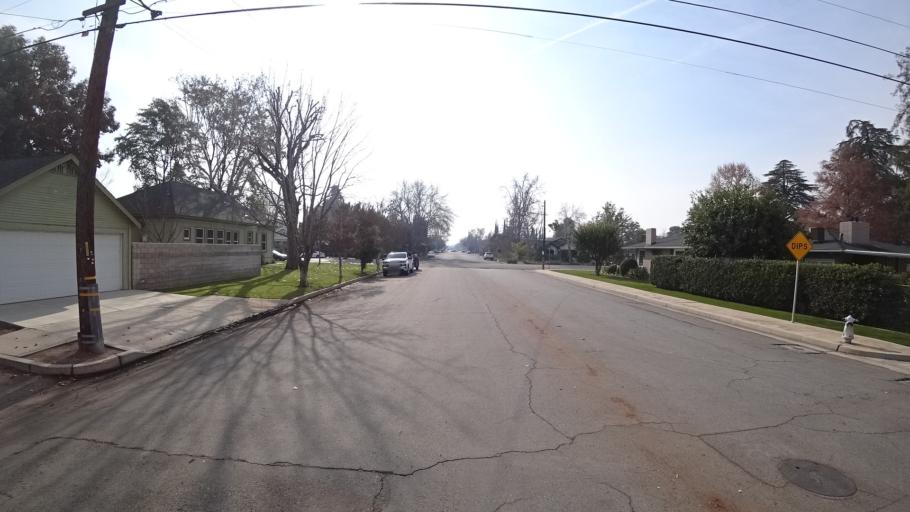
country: US
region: California
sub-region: Kern County
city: Bakersfield
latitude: 35.3777
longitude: -119.0340
